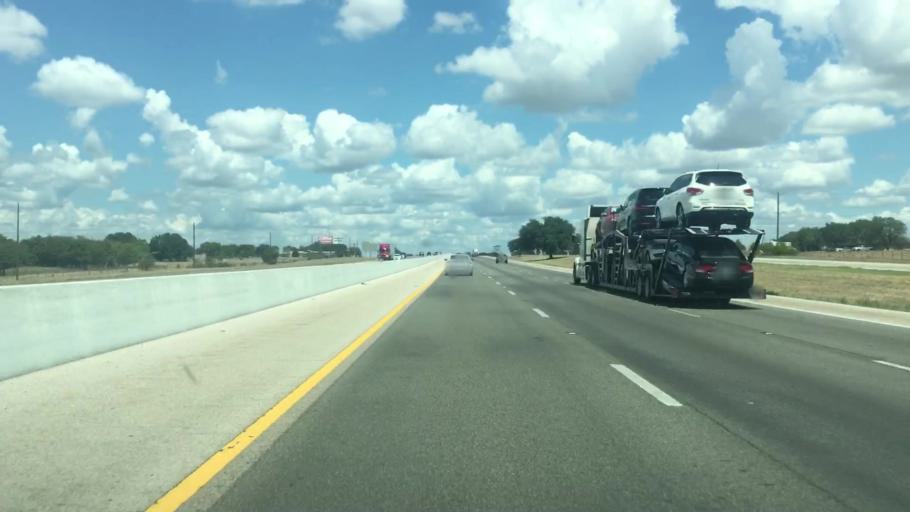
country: US
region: Texas
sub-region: Williamson County
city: Serenada
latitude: 30.7834
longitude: -97.6243
